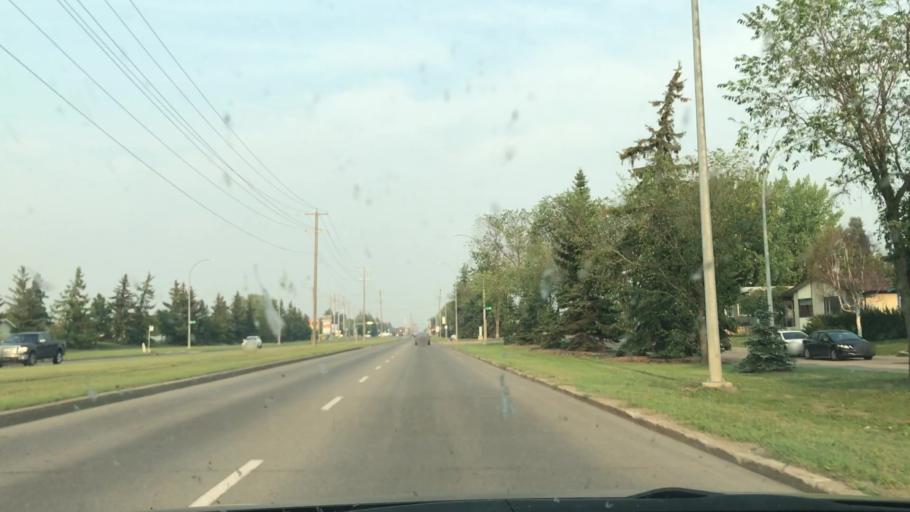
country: CA
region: Alberta
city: Edmonton
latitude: 53.5994
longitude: -113.5233
